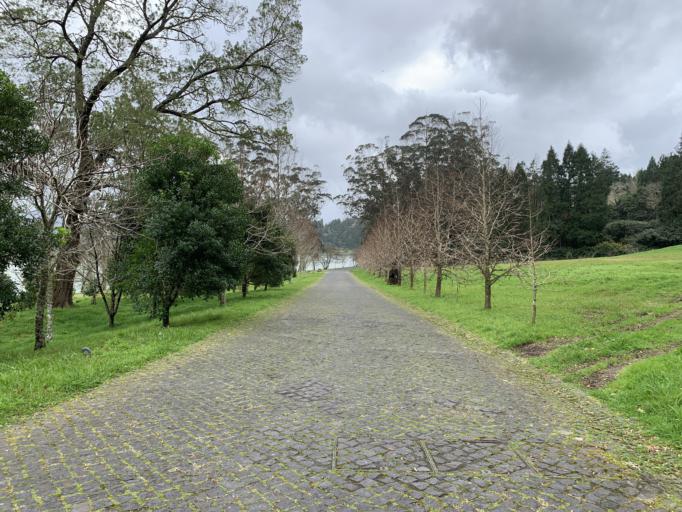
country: PT
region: Azores
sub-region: Povoacao
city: Furnas
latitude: 37.7507
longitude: -25.3371
